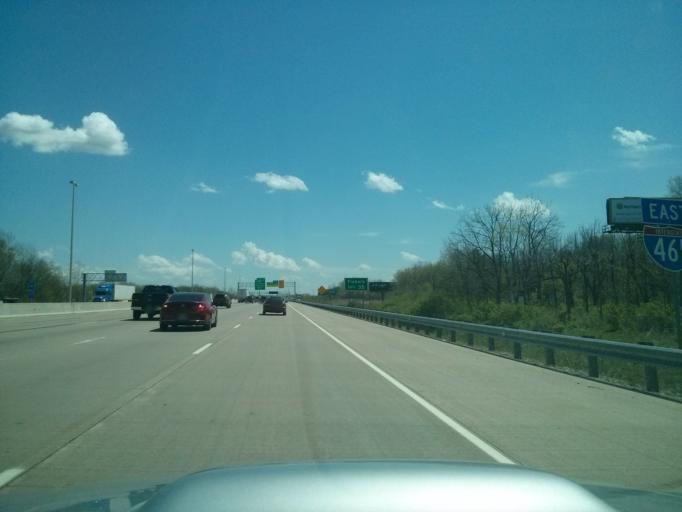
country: US
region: Indiana
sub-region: Hamilton County
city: Carmel
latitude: 39.9171
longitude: -86.0979
